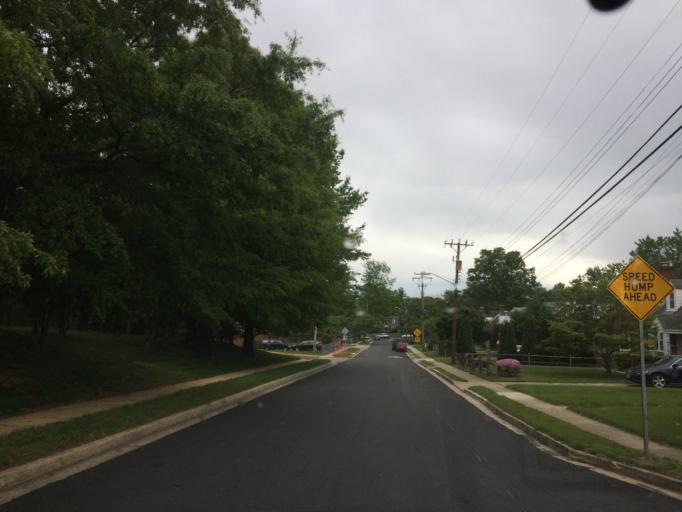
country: US
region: Virginia
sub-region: Fairfax County
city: Jefferson
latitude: 38.8752
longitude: -77.1996
